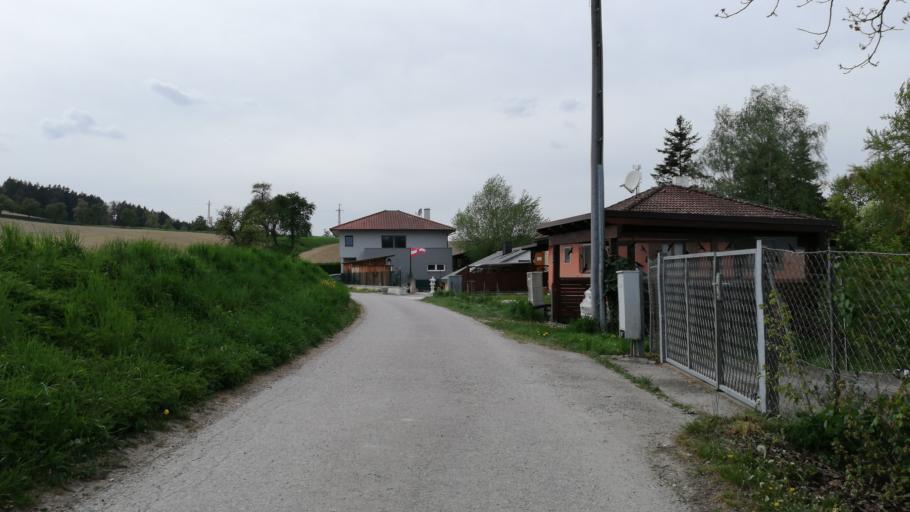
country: AT
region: Upper Austria
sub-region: Politischer Bezirk Grieskirchen
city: Bad Schallerbach
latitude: 48.1866
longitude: 13.9453
